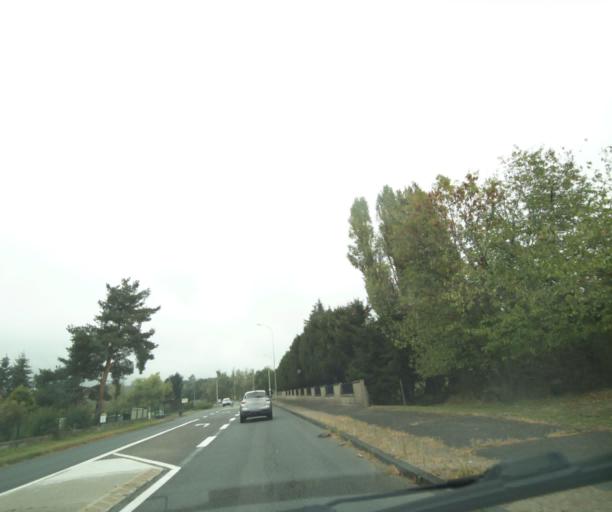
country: FR
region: Auvergne
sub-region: Departement du Puy-de-Dome
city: Saint-Genes-Champanelle
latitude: 45.7040
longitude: 3.0426
